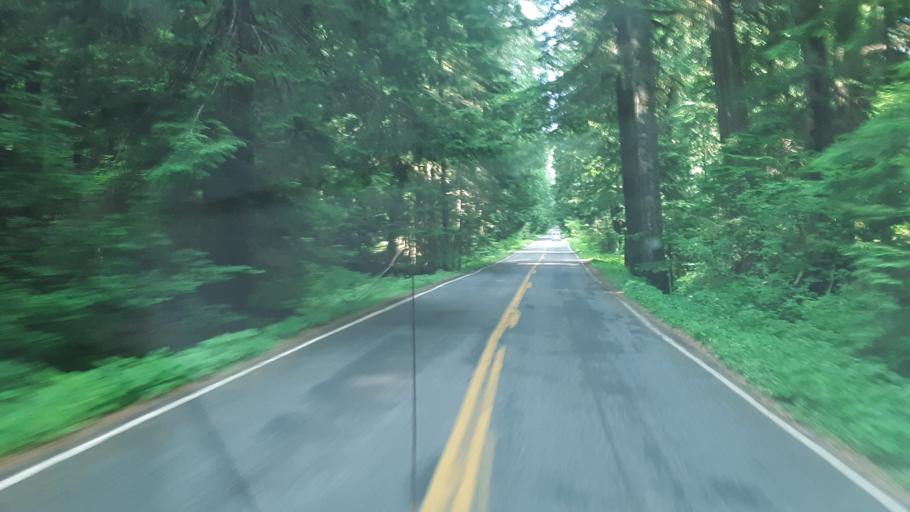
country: US
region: Washington
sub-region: Pierce County
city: Buckley
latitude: 46.7703
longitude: -121.5483
